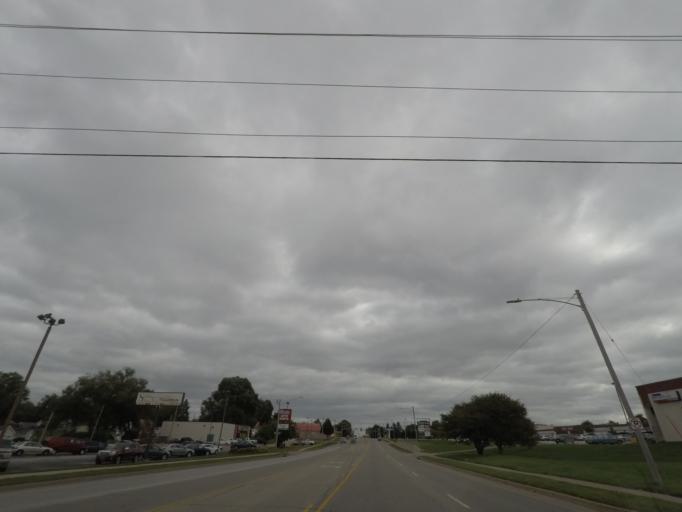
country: US
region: Iowa
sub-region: Polk County
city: Des Moines
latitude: 41.5265
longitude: -93.6199
